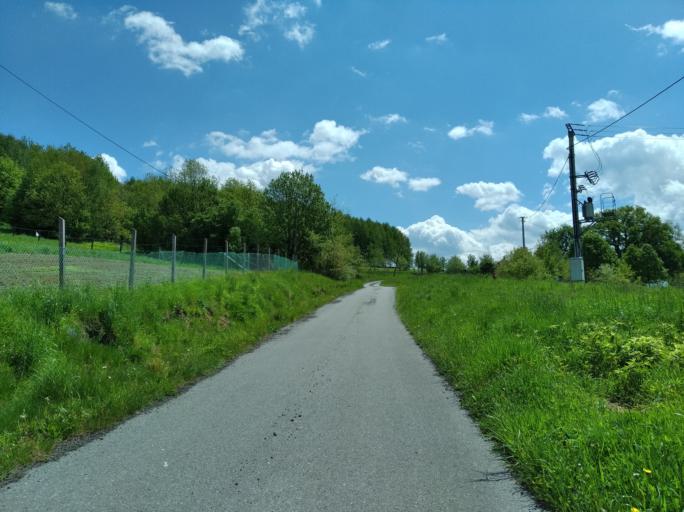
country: PL
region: Subcarpathian Voivodeship
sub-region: Powiat strzyzowski
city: Wisniowa
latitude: 49.8403
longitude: 21.6444
